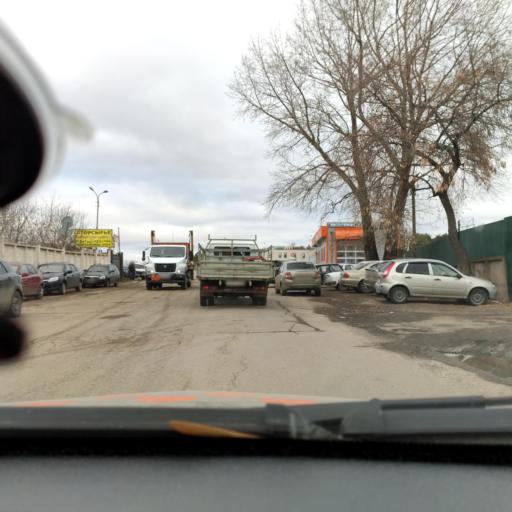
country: RU
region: Bashkortostan
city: Ufa
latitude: 54.7514
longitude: 55.9807
